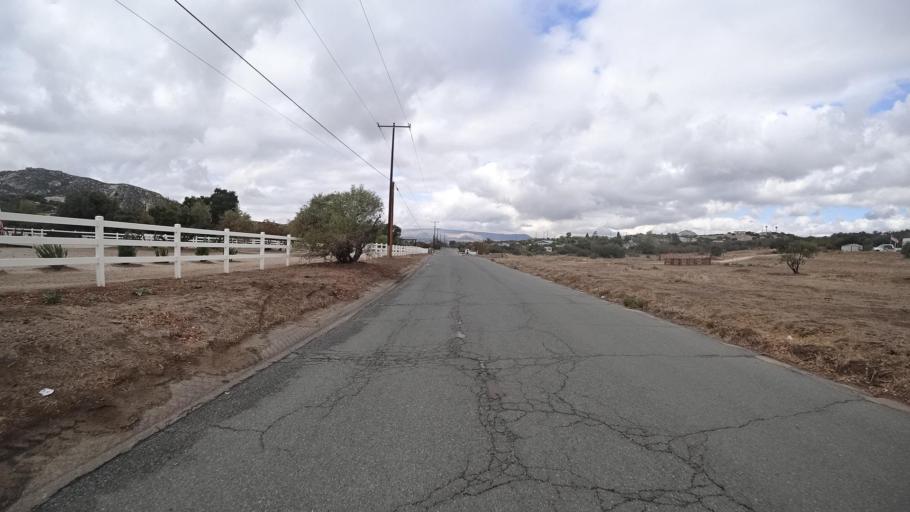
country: US
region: California
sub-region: San Diego County
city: Campo
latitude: 32.6300
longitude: -116.4199
